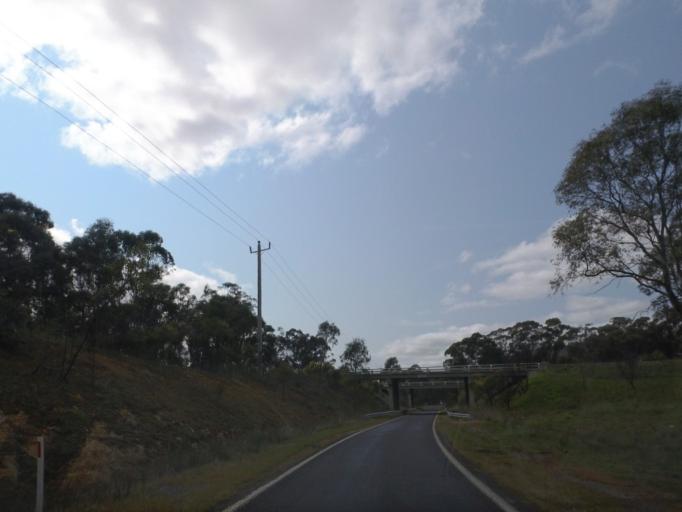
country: AU
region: Victoria
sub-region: Murrindindi
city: Kinglake West
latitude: -37.1078
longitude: 145.0909
